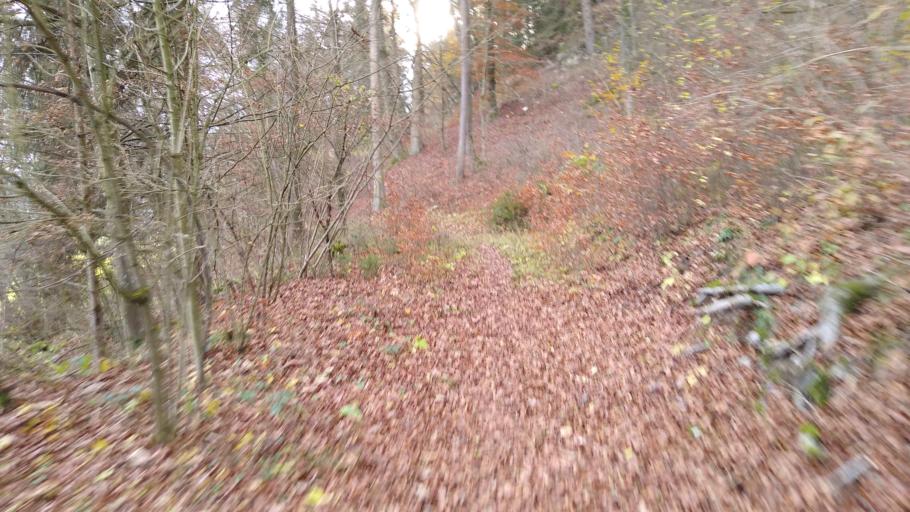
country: DE
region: Bavaria
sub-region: Upper Palatinate
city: Dietfurt
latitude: 49.0702
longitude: 11.6230
